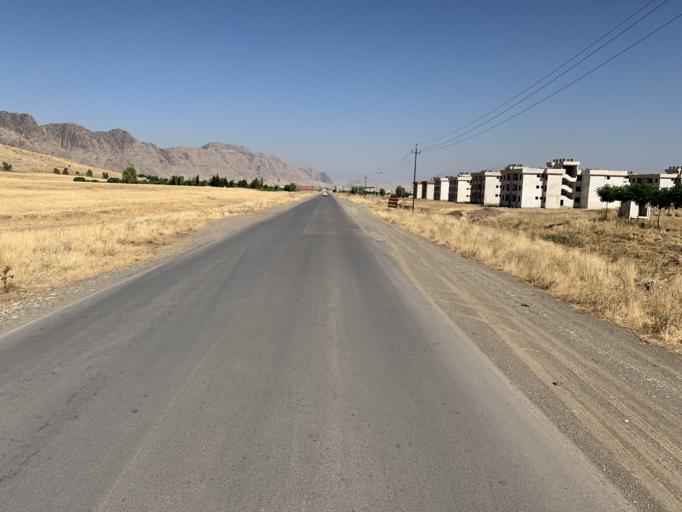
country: IQ
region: As Sulaymaniyah
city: Raniye
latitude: 36.2651
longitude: 44.8429
